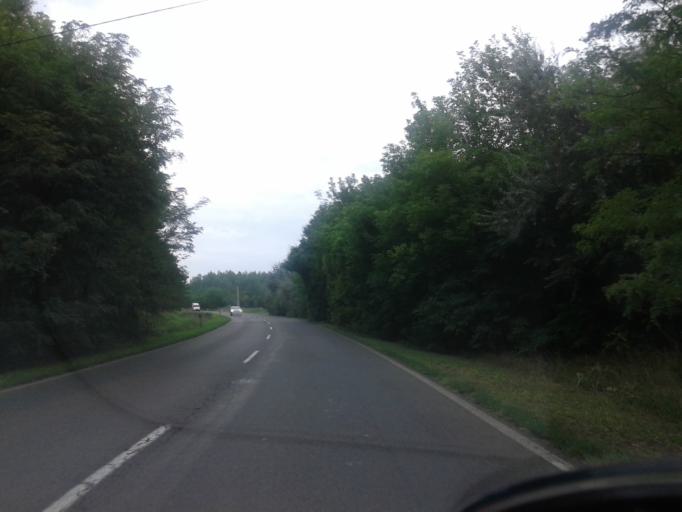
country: HU
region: Csongrad
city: Asotthalom
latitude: 46.2294
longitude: 19.7540
